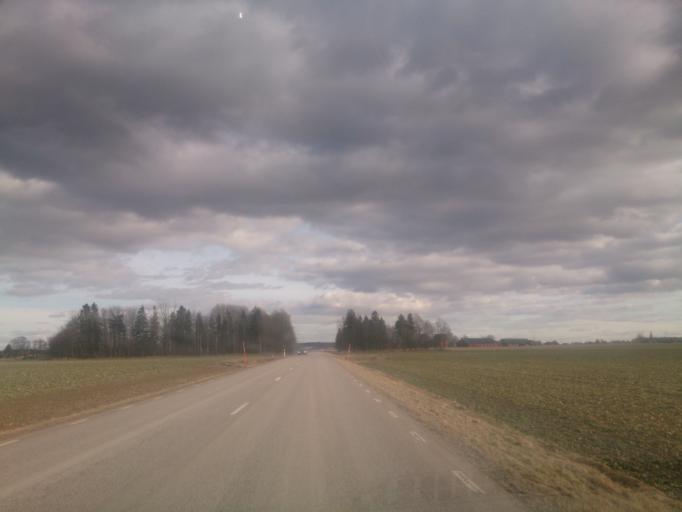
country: SE
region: OEstergoetland
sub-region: Motala Kommun
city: Borensberg
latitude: 58.5162
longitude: 15.1806
